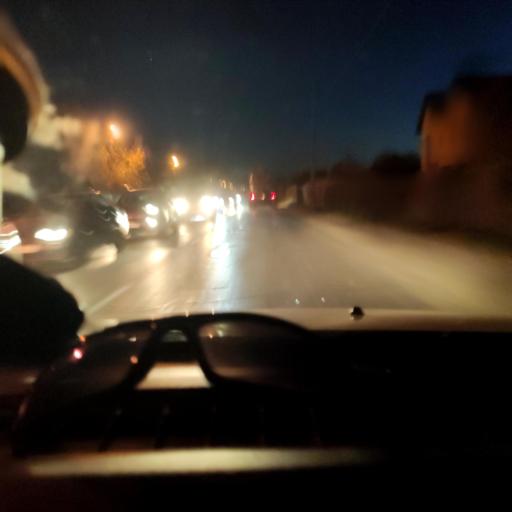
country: RU
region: Samara
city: Rozhdestveno
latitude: 53.1492
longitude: 50.0694
